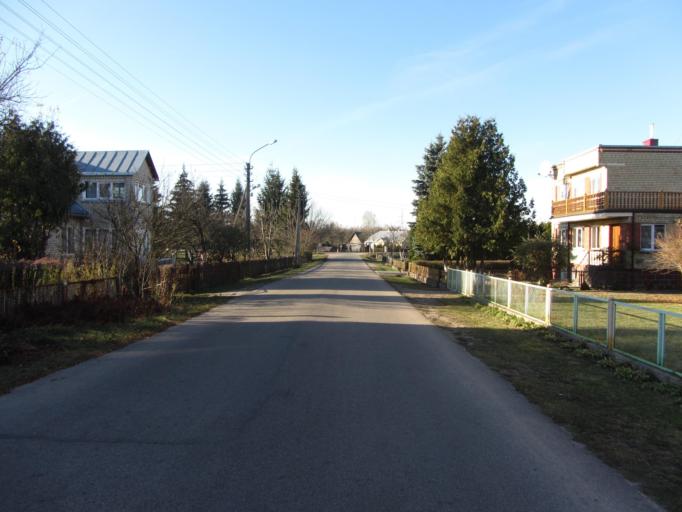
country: LT
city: Eisiskes
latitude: 54.1833
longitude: 25.0023
